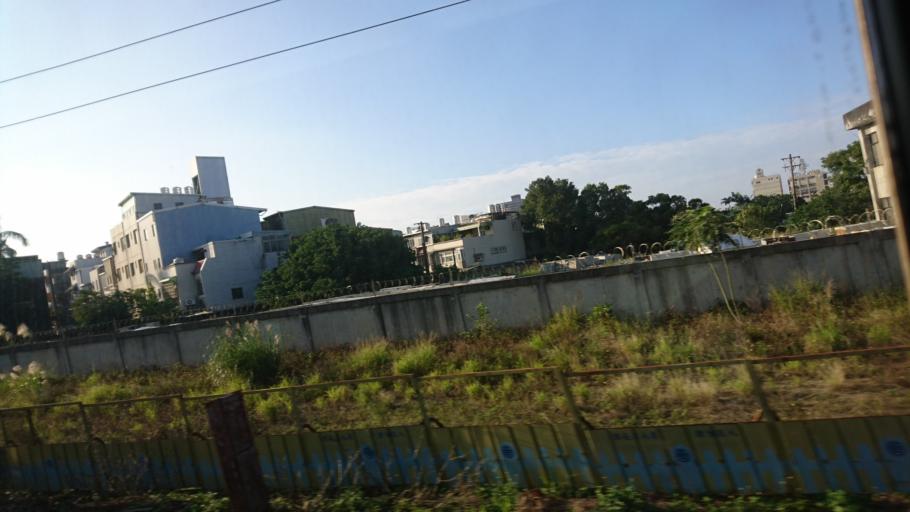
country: TW
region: Taiwan
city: Taoyuan City
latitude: 24.9612
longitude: 121.2421
